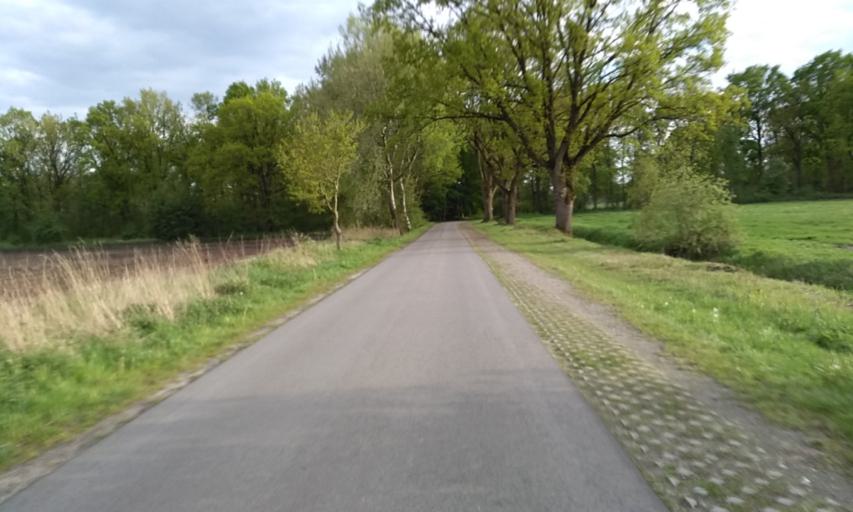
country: DE
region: Lower Saxony
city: Sauensiek
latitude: 53.3932
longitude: 9.5626
